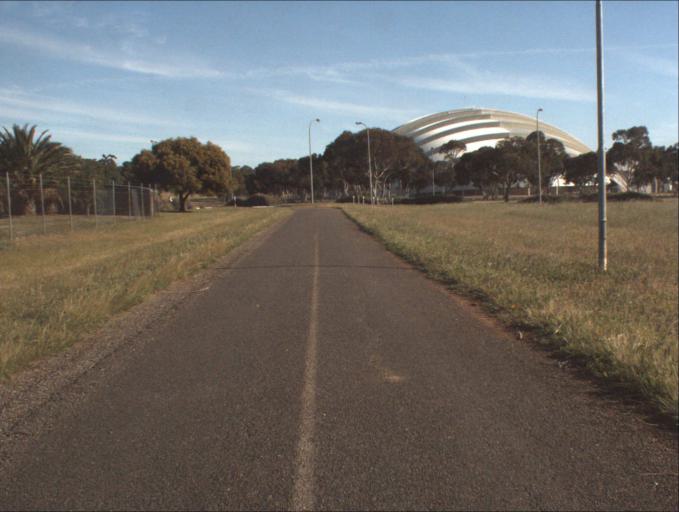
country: AU
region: South Australia
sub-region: Port Adelaide Enfield
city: Enfield
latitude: -34.8390
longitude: 138.6135
